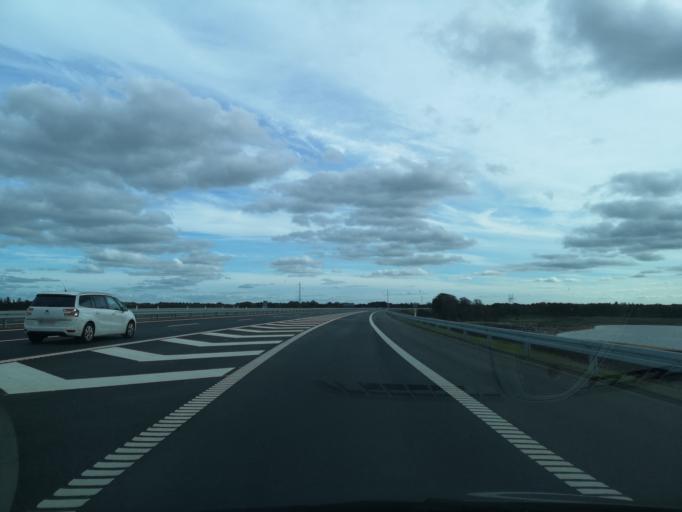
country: DK
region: Central Jutland
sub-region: Holstebro Kommune
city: Holstebro
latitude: 56.3669
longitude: 8.7220
